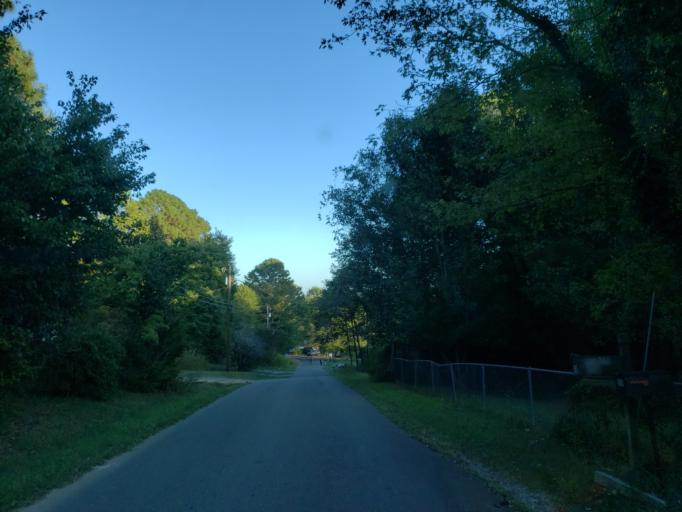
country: US
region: Georgia
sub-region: Pickens County
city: Jasper
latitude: 34.4548
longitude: -84.4439
